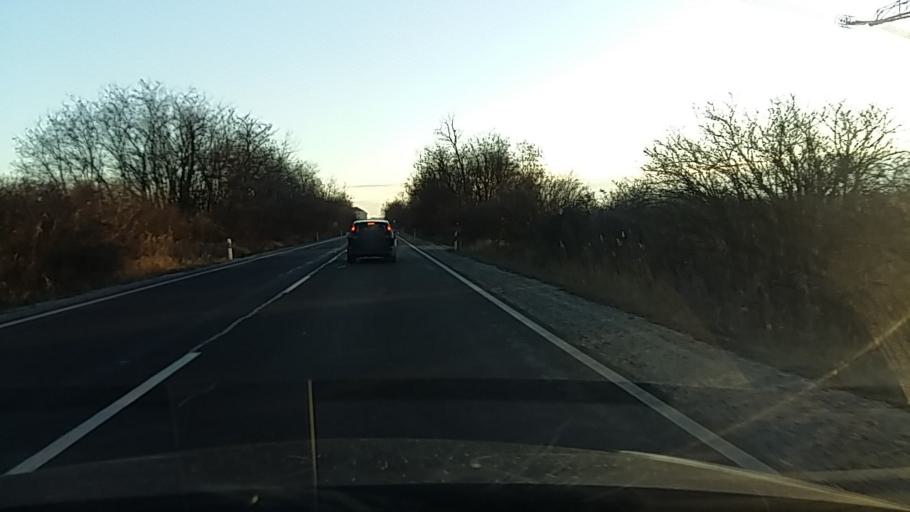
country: HU
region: Hajdu-Bihar
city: Teglas
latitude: 47.7457
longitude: 21.6780
